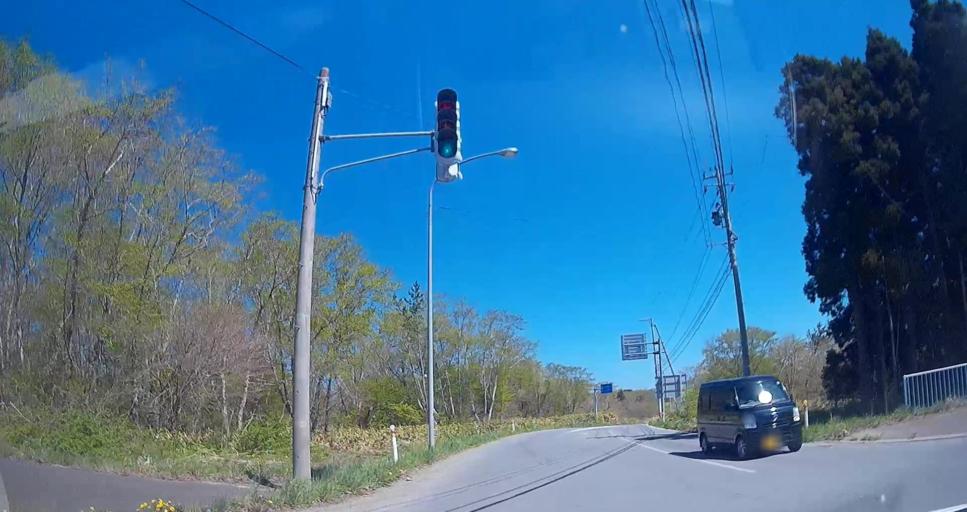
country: JP
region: Aomori
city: Misawa
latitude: 40.9133
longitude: 141.3730
